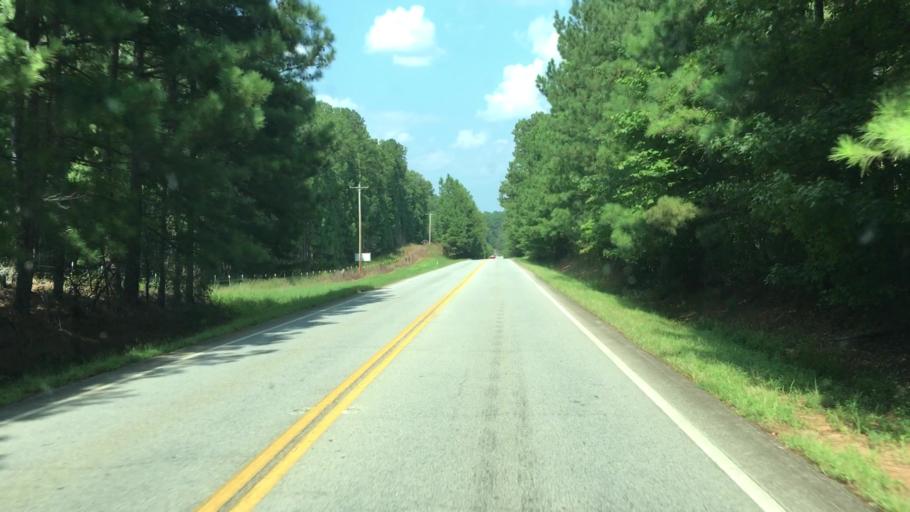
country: US
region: Georgia
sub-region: Butts County
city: Indian Springs
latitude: 33.1364
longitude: -83.8626
